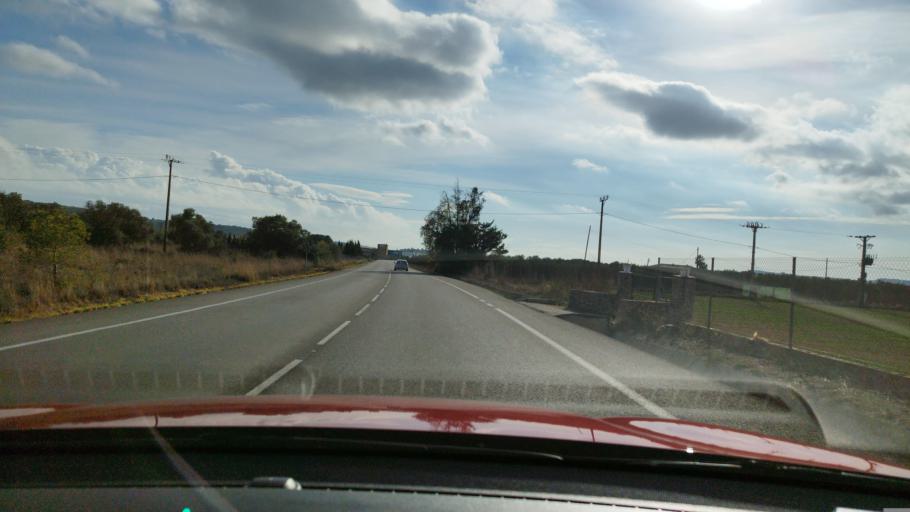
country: ES
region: Catalonia
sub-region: Provincia de Tarragona
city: Santa Oliva
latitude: 41.2460
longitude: 1.5451
